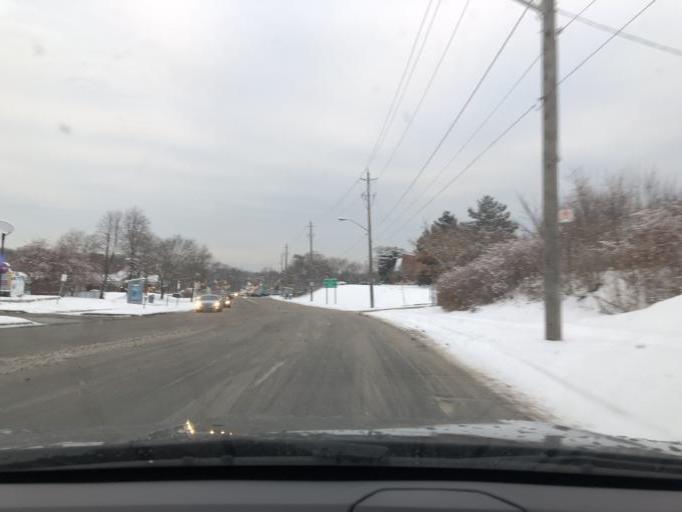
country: CA
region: Ontario
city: Toronto
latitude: 43.6963
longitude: -79.4901
